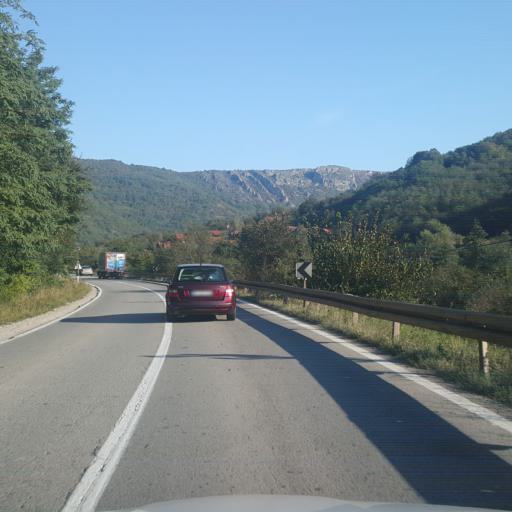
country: RS
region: Central Serbia
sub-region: Nisavski Okrug
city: Niska Banja
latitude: 43.3152
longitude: 22.0538
